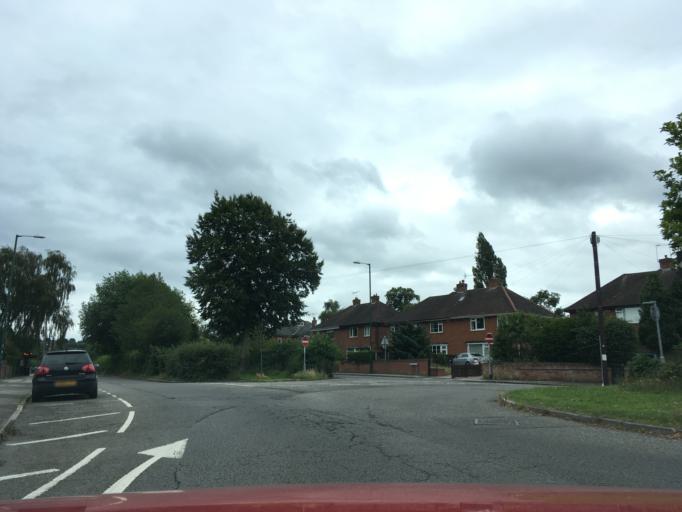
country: GB
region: England
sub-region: Nottinghamshire
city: Arnold
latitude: 52.9852
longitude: -1.1473
